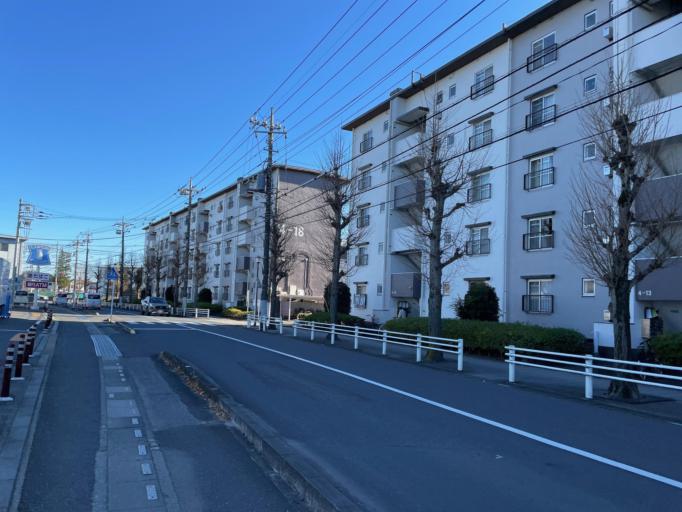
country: JP
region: Saitama
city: Ageoshimo
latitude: 35.9666
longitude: 139.6310
